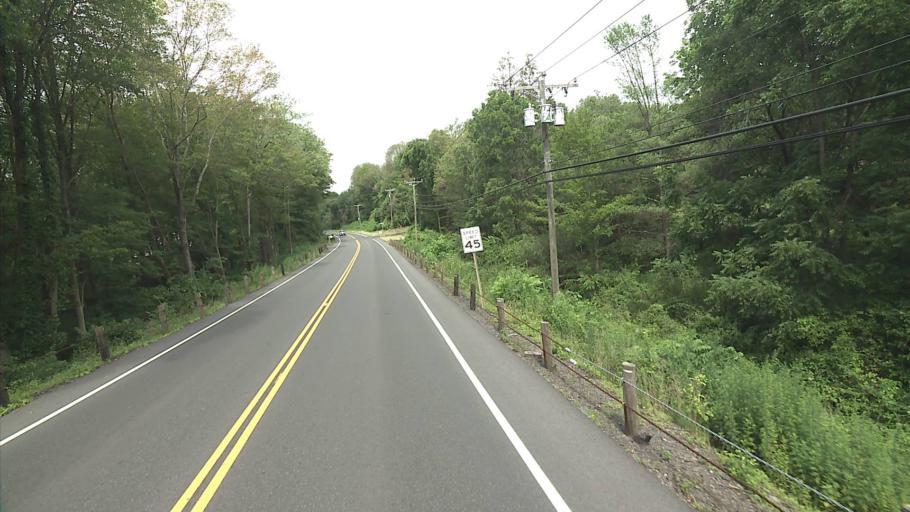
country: US
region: Connecticut
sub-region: New Haven County
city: Southbury
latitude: 41.4752
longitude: -73.1923
